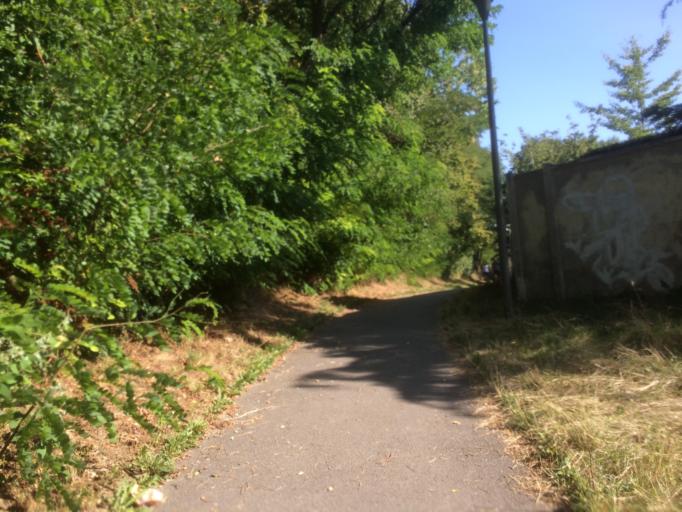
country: FR
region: Ile-de-France
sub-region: Departement de l'Essonne
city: Epinay-sur-Orge
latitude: 48.6846
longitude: 2.3180
